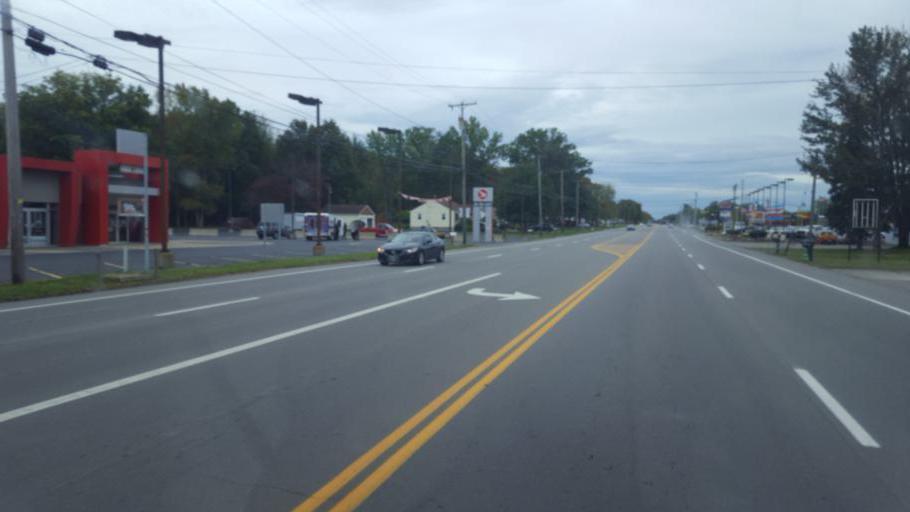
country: US
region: Ohio
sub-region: Lorain County
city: Amherst
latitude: 41.3878
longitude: -82.2099
